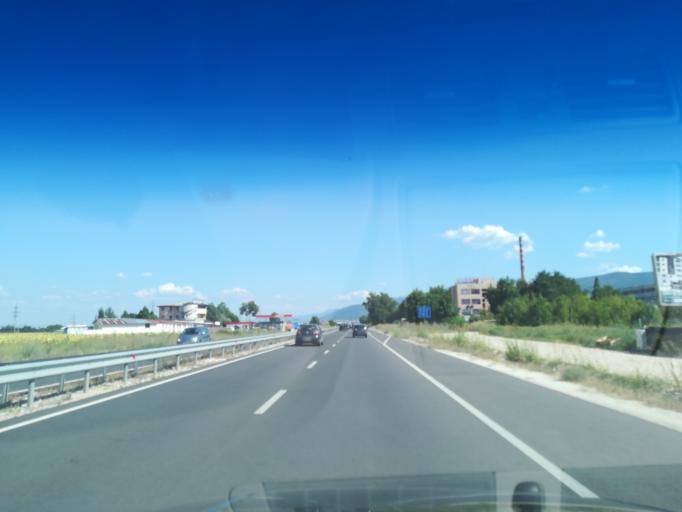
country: BG
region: Plovdiv
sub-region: Obshtina Asenovgrad
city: Asenovgrad
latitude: 42.0696
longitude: 24.8121
